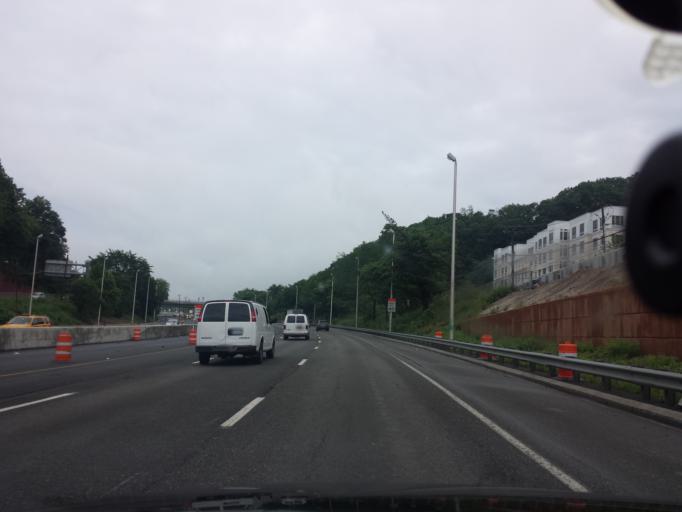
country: US
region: New Jersey
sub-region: Hudson County
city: Bayonne
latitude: 40.6105
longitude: -74.0937
